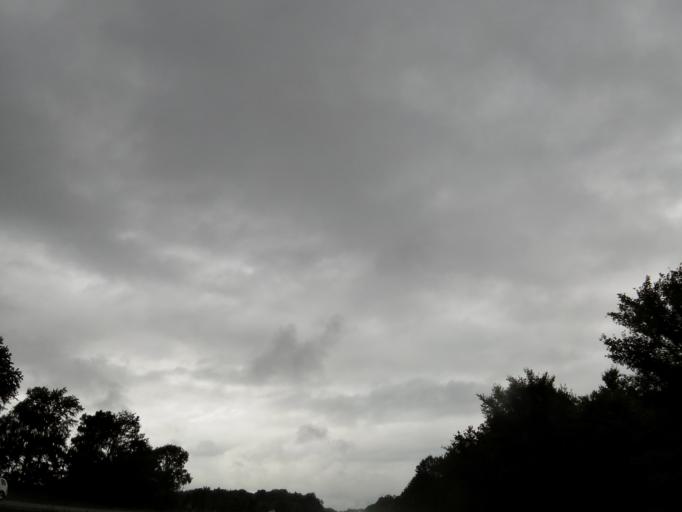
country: US
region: Illinois
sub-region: Jefferson County
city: Mount Vernon
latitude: 38.3485
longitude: -88.9821
